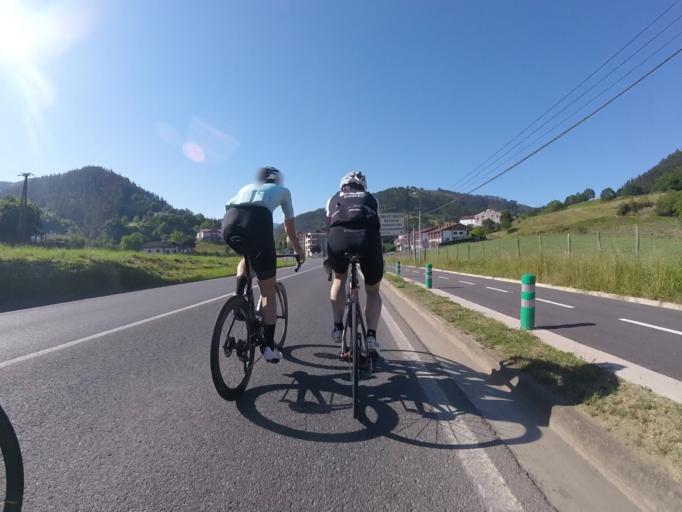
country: ES
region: Basque Country
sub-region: Provincia de Guipuzcoa
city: Azpeitia
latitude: 43.1607
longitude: -2.2455
